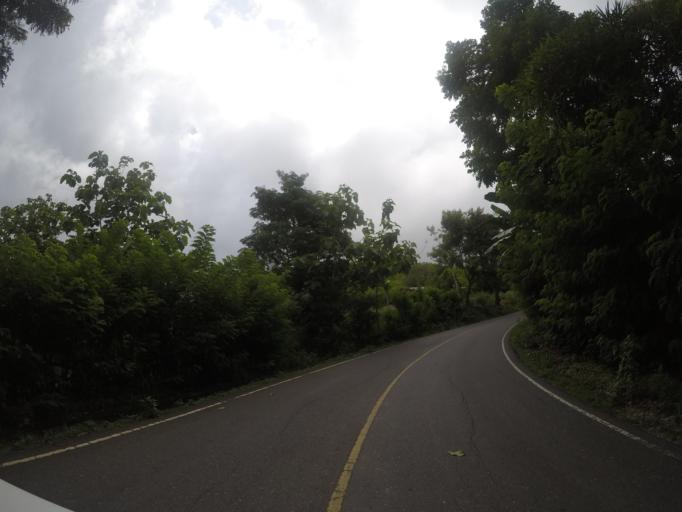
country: TL
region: Bobonaro
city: Maliana
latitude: -8.9696
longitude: 125.0495
